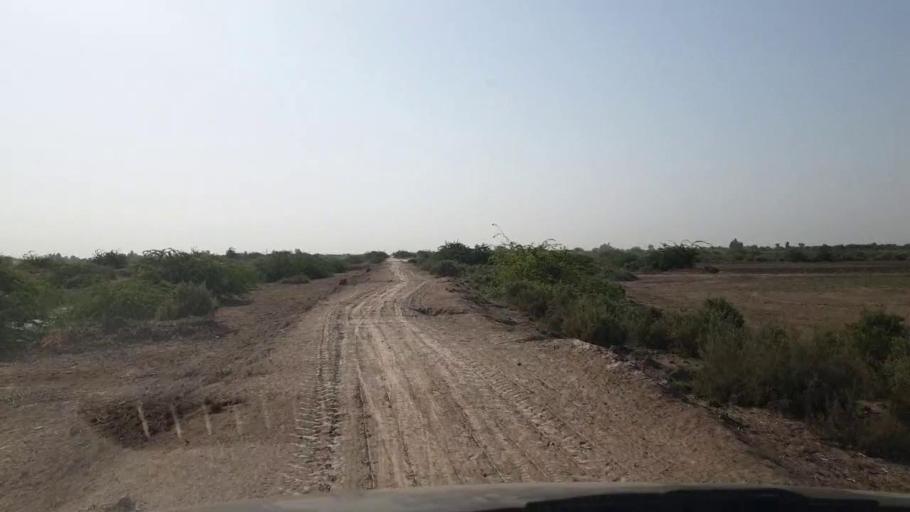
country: PK
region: Sindh
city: Kadhan
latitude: 24.5816
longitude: 69.0794
